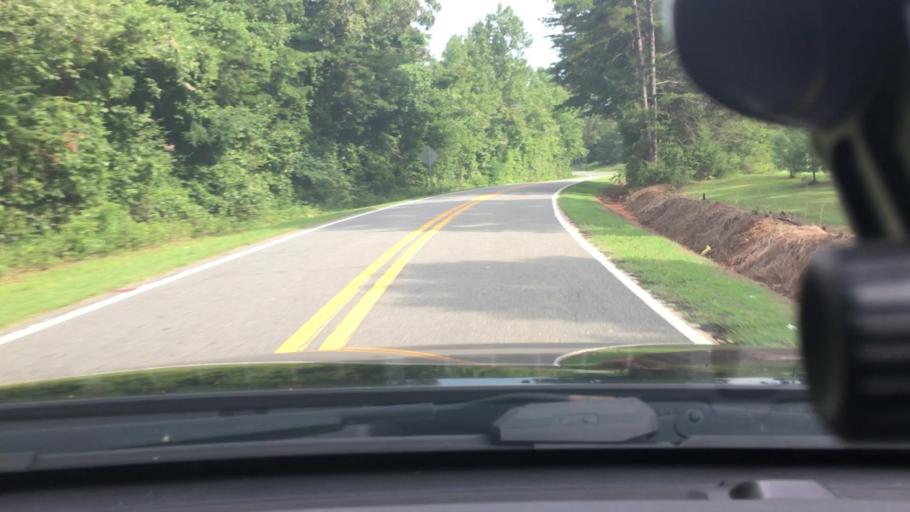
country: US
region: North Carolina
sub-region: Rutherford County
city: Rutherfordton
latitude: 35.4024
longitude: -81.9740
